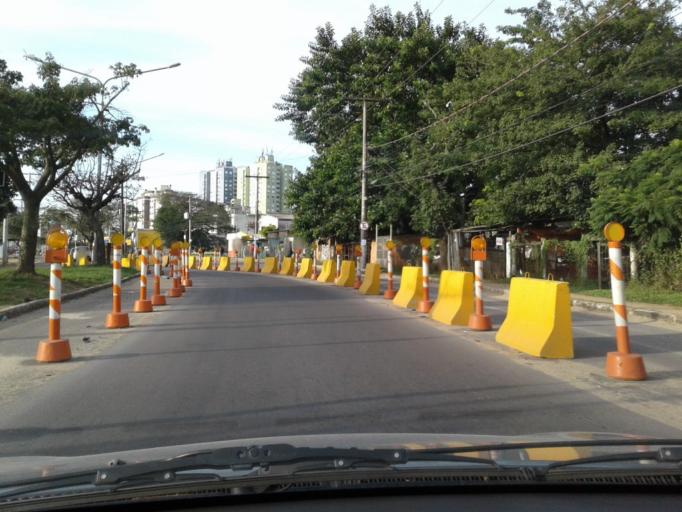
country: BR
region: Rio Grande do Sul
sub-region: Porto Alegre
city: Porto Alegre
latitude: -30.0940
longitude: -51.2433
